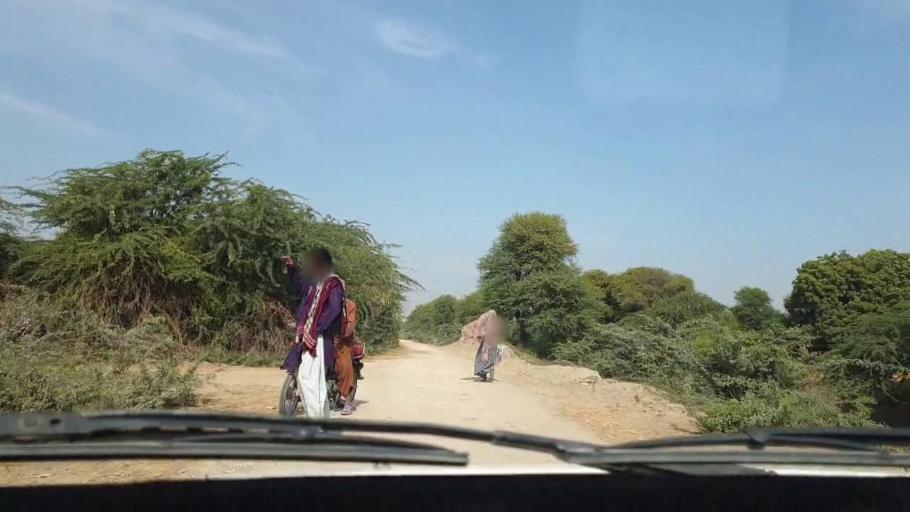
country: PK
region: Sindh
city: Bulri
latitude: 24.8895
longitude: 68.4630
